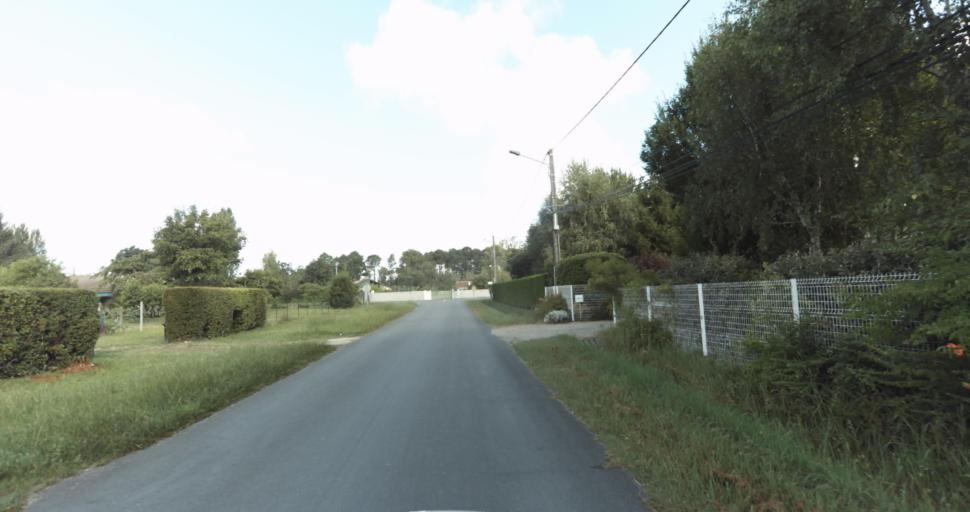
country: FR
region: Aquitaine
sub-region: Departement de la Gironde
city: Bazas
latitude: 44.4395
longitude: -0.2471
